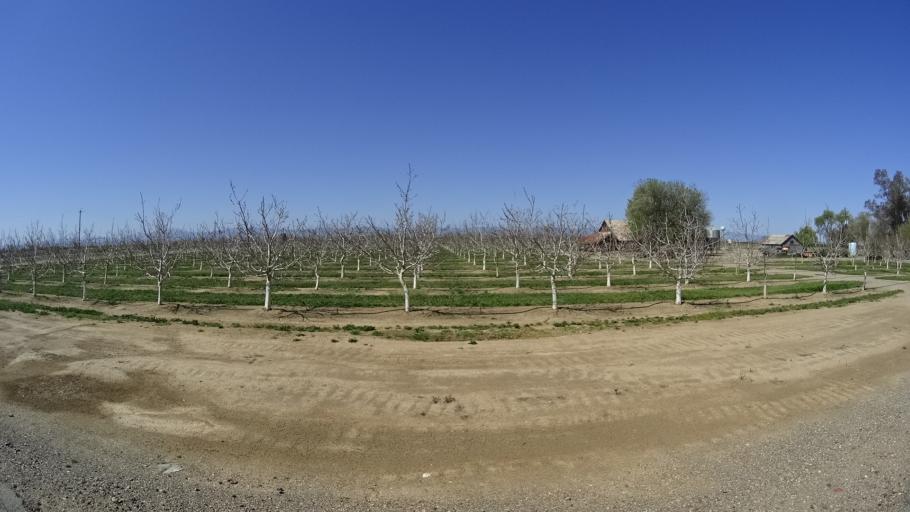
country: US
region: California
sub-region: Glenn County
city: Orland
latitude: 39.6763
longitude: -122.2343
